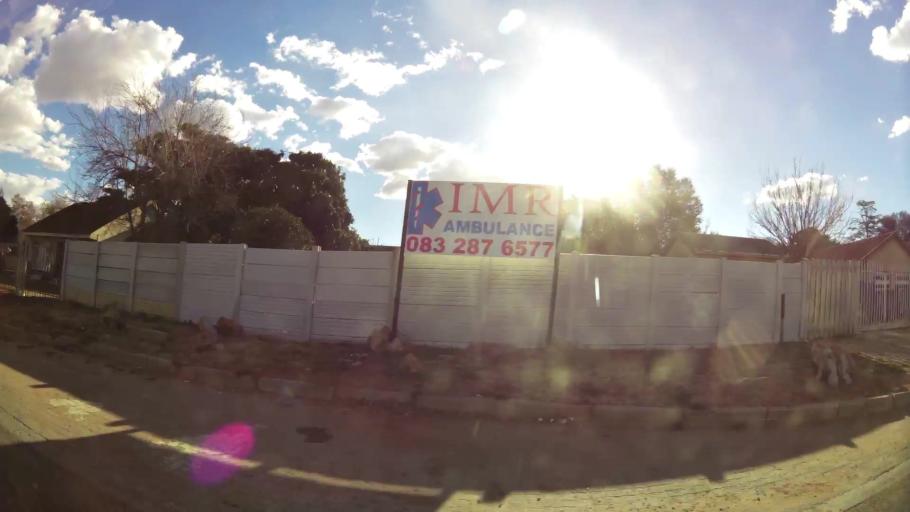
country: ZA
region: North-West
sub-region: Dr Kenneth Kaunda District Municipality
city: Klerksdorp
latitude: -26.8416
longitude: 26.6570
